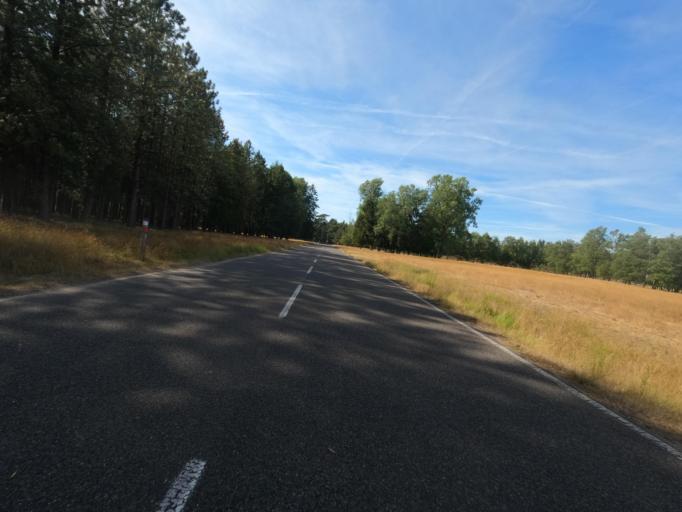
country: DE
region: North Rhine-Westphalia
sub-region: Regierungsbezirk Dusseldorf
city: Bruggen
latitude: 51.2655
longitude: 6.1468
